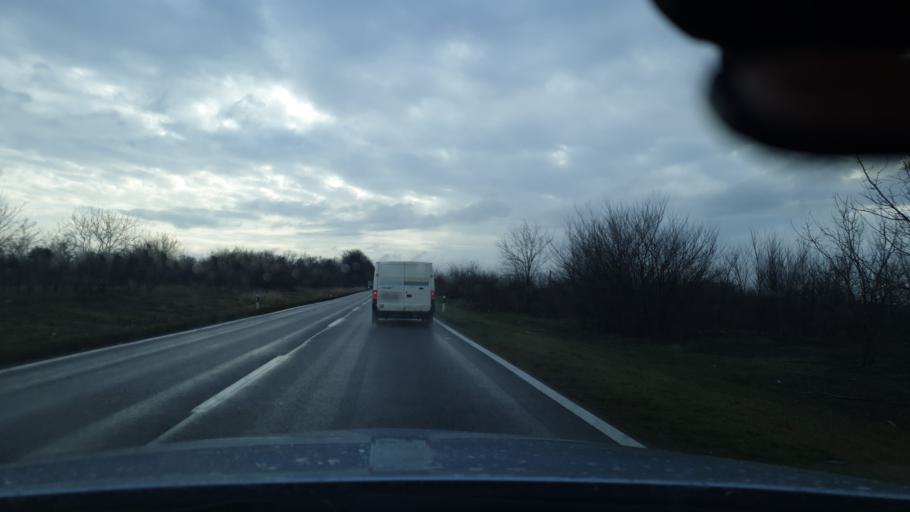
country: RS
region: Autonomna Pokrajina Vojvodina
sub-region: Juznobanatski Okrug
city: Kovin
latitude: 44.7616
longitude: 20.9572
